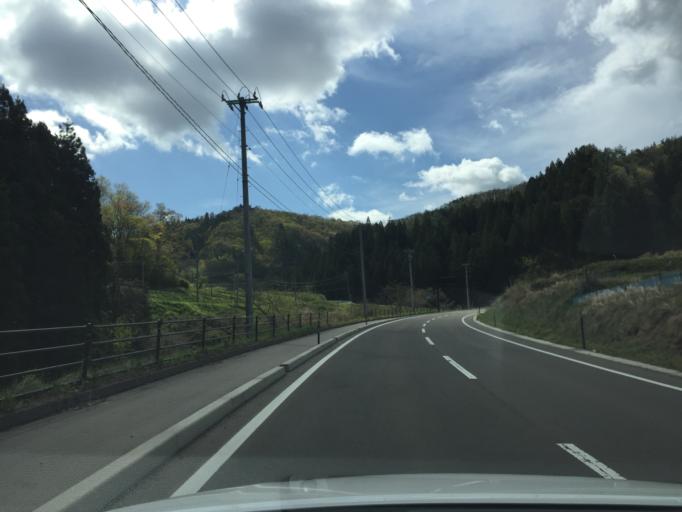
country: JP
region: Fukushima
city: Hobaramachi
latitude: 37.6399
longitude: 140.6426
